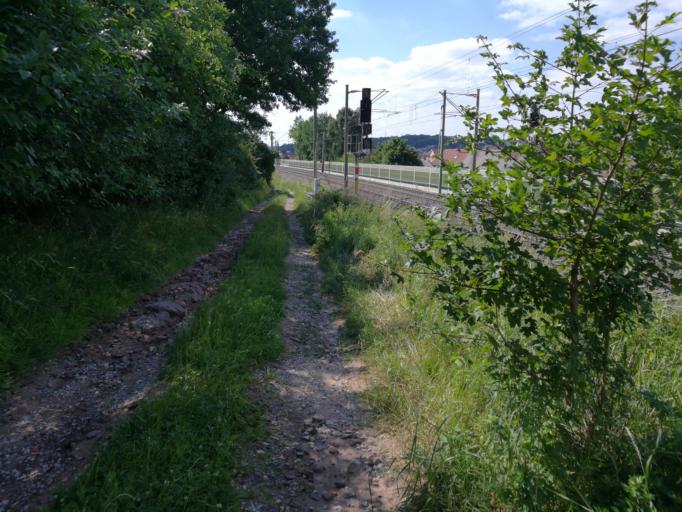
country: DE
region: Bavaria
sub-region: Regierungsbezirk Mittelfranken
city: Veitsbronn
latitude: 49.5053
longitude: 10.8864
